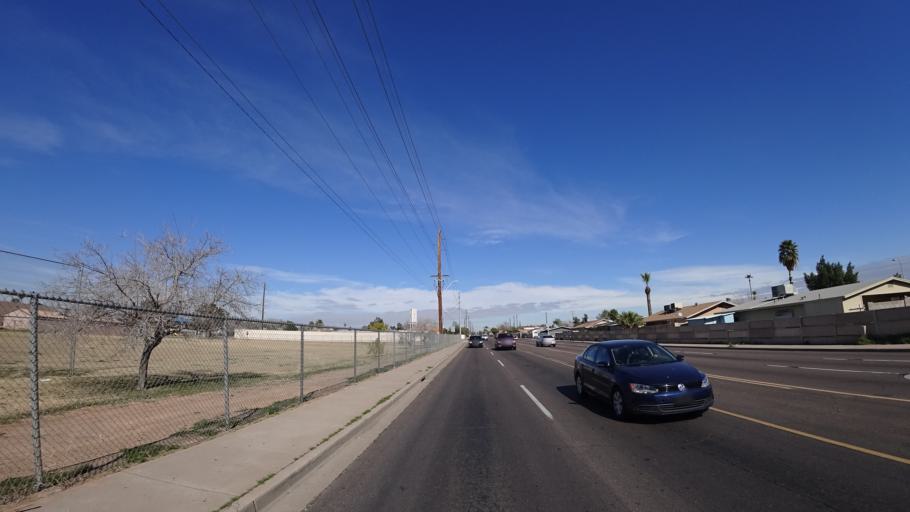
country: US
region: Arizona
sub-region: Maricopa County
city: Glendale
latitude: 33.4753
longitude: -112.1865
